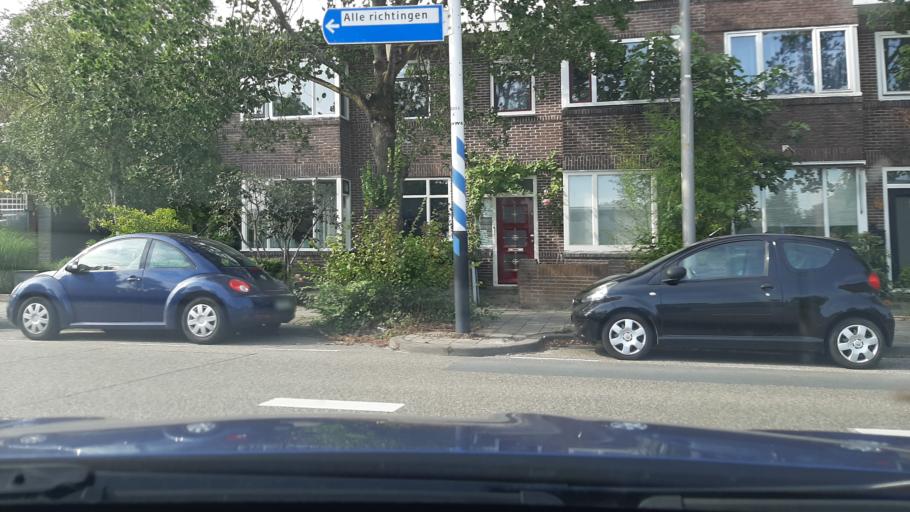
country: NL
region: Friesland
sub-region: Gemeente Leeuwarden
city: Huizum
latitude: 53.1909
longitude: 5.8017
